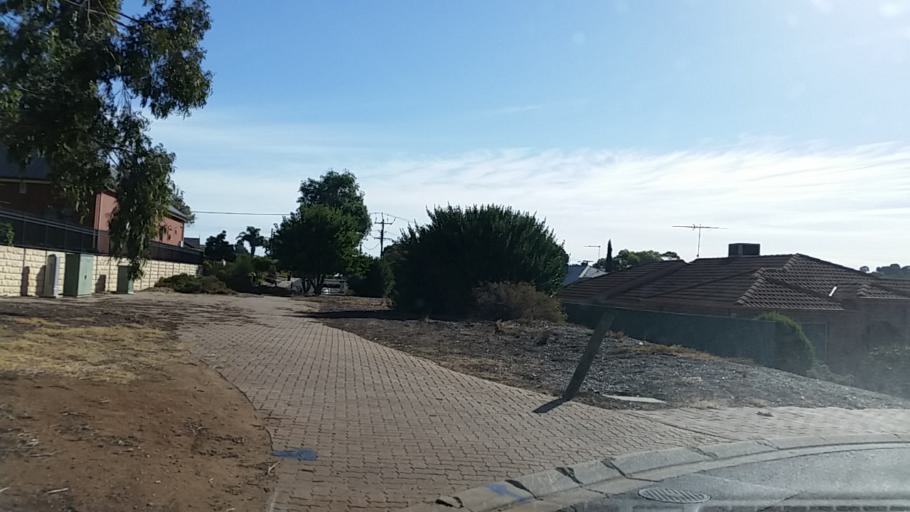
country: AU
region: South Australia
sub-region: Campbelltown
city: Athelstone
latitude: -34.8620
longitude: 138.7111
